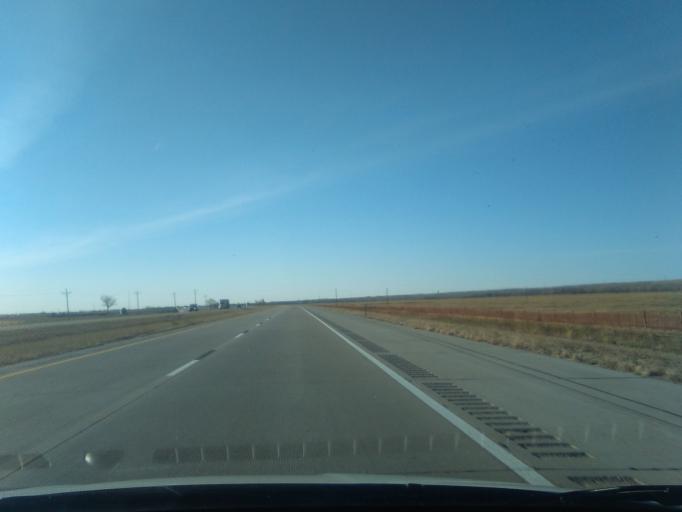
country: US
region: Colorado
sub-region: Sedgwick County
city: Julesburg
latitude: 41.0626
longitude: -102.0110
